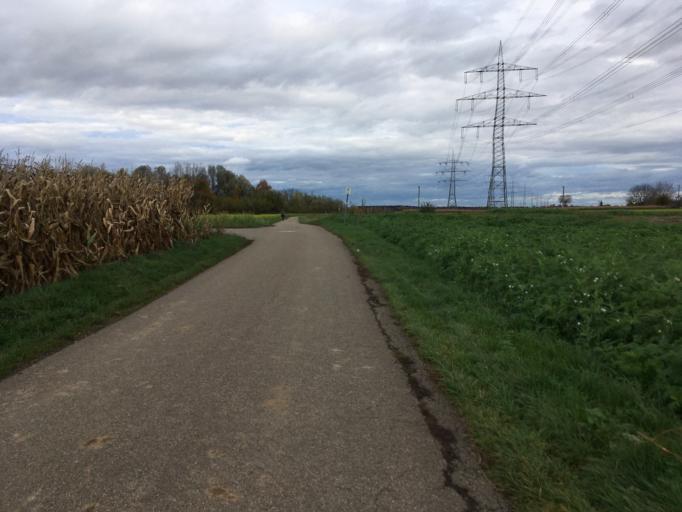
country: DE
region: Baden-Wuerttemberg
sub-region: Freiburg Region
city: Riegel
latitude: 48.1495
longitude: 7.7361
